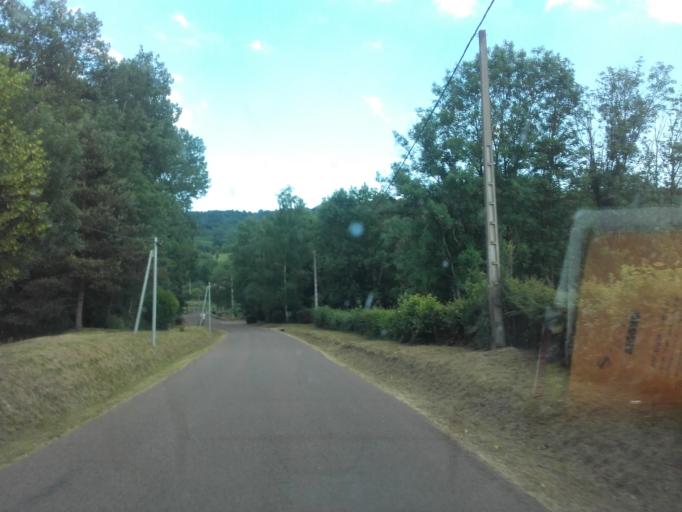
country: FR
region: Bourgogne
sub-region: Departement de Saone-et-Loire
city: Saint-Leger-sur-Dheune
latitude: 46.8918
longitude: 4.6779
